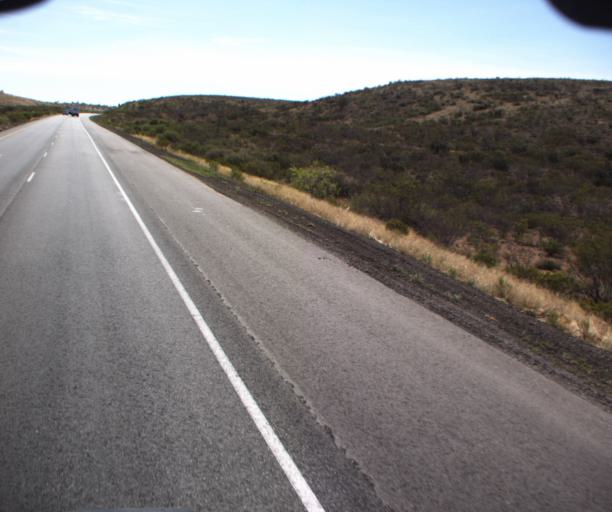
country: US
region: Arizona
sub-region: Cochise County
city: Mescal
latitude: 31.9689
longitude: -110.4761
